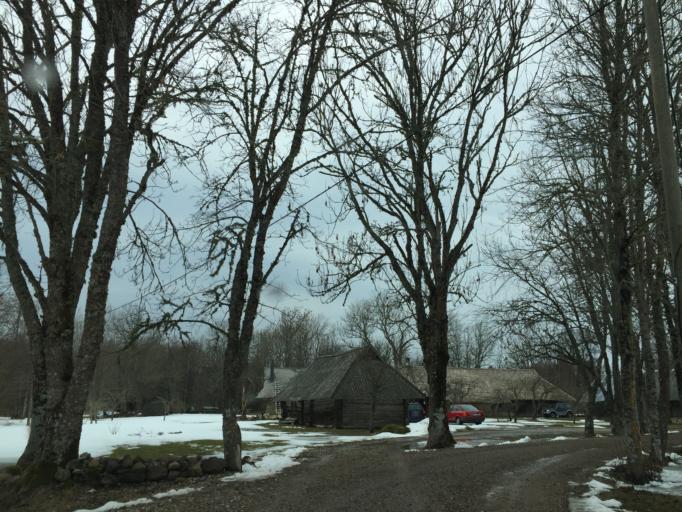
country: EE
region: Saare
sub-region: Kuressaare linn
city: Kuressaare
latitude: 58.4406
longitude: 22.1422
